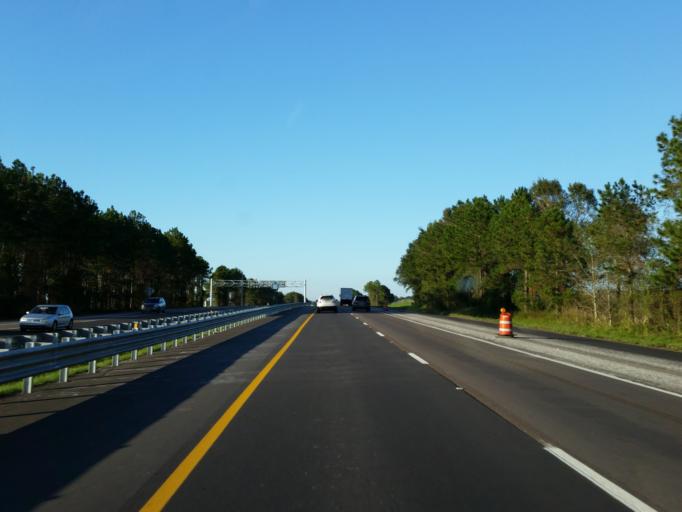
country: US
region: Florida
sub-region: Pasco County
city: San Antonio
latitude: 28.3617
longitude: -82.3195
